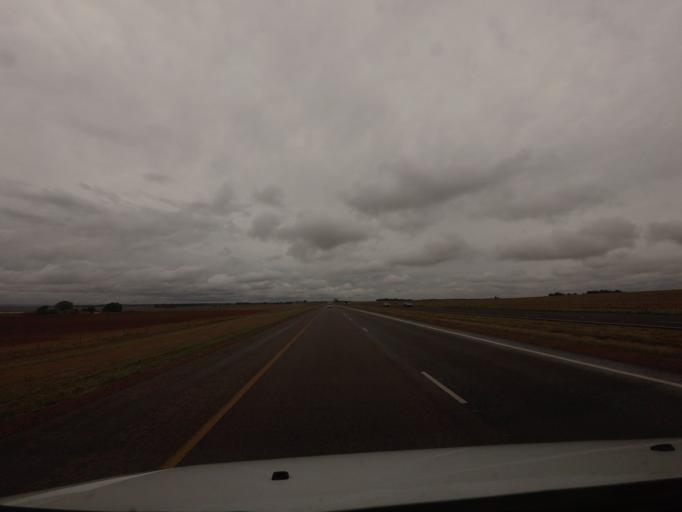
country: ZA
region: Mpumalanga
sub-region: Nkangala District Municipality
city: Middelburg
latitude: -25.8195
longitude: 29.6201
